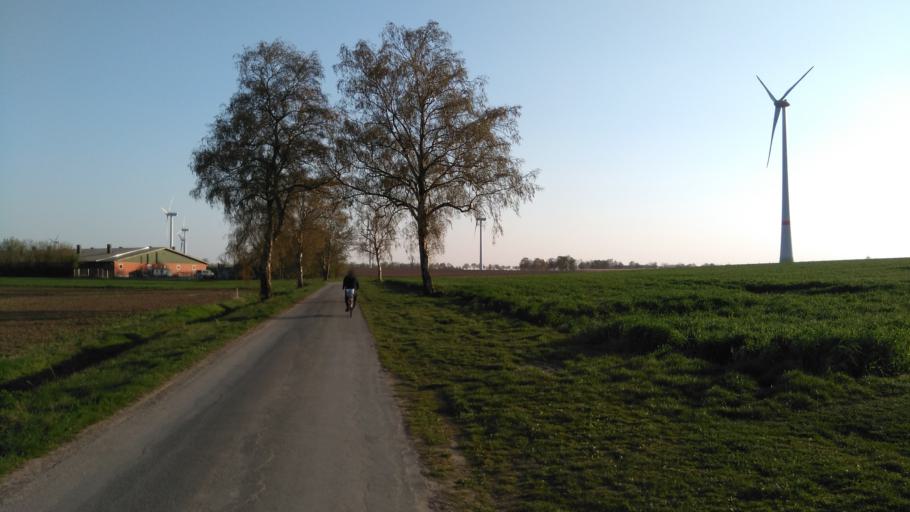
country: DE
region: Lower Saxony
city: Nottensdorf
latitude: 53.4652
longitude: 9.5884
